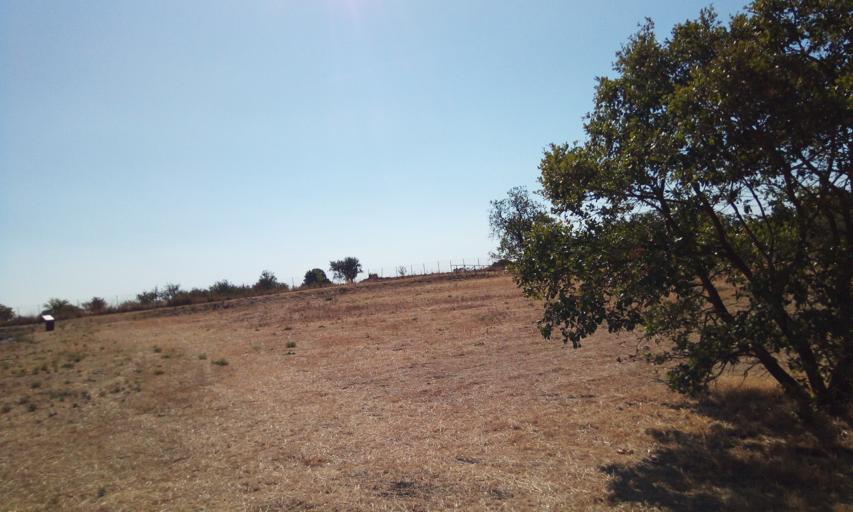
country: IT
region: Apulia
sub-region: Provincia di Bari
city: Gioia del Colle
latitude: 40.8325
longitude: 16.9672
